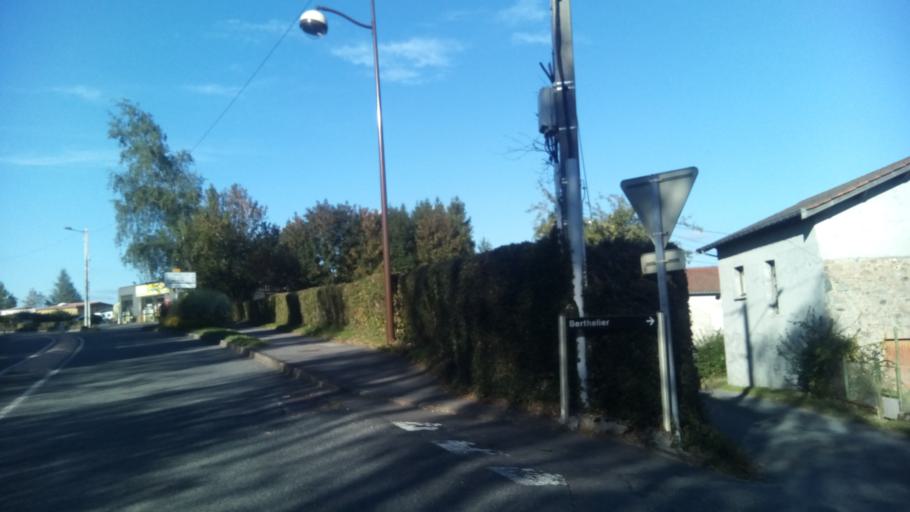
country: FR
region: Rhone-Alpes
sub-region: Departement de la Loire
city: Belmont-de-la-Loire
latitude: 46.1940
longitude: 4.4378
